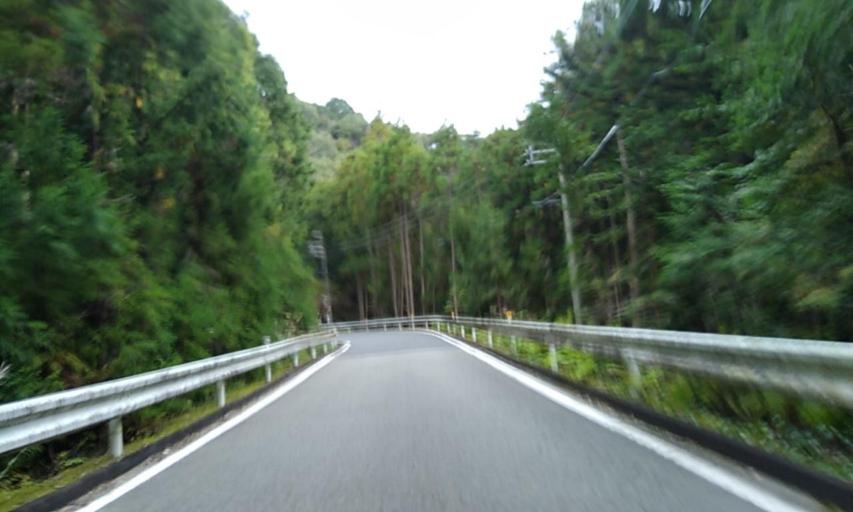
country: JP
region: Wakayama
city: Shingu
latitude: 33.5419
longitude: 135.8415
